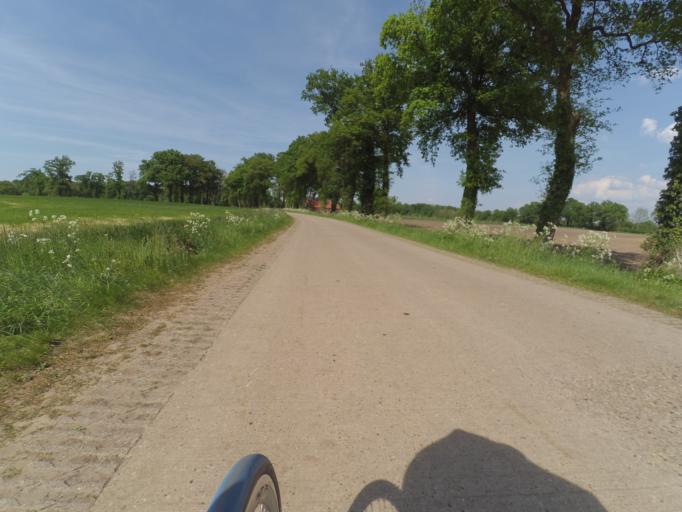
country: NL
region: Overijssel
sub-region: Gemeente Tubbergen
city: Tubbergen
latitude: 52.3509
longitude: 6.8014
